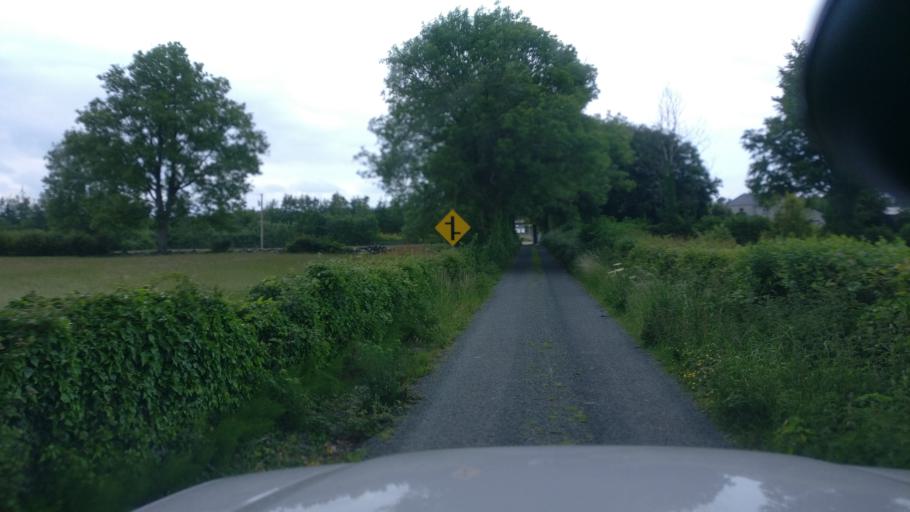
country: IE
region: Connaught
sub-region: County Galway
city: Ballinasloe
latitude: 53.3100
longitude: -8.2593
